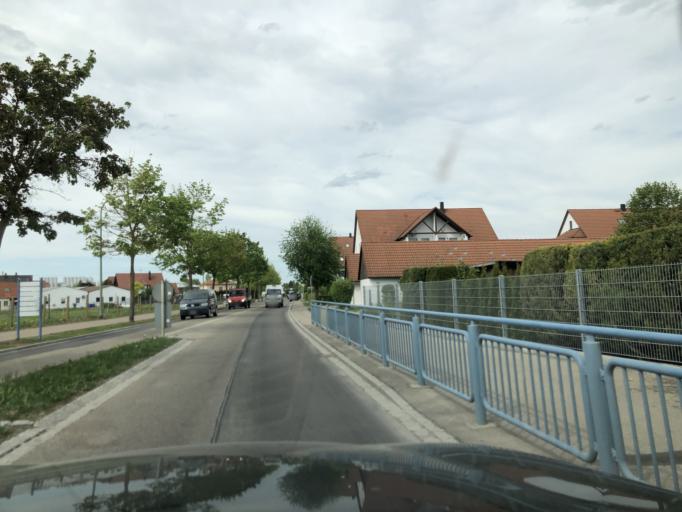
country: DE
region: Bavaria
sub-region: Swabia
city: Mertingen
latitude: 48.6574
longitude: 10.8146
